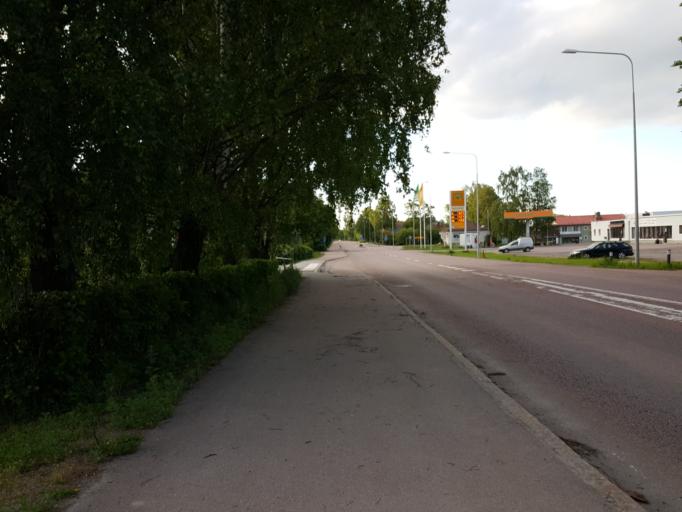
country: SE
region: Uppsala
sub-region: Osthammars Kommun
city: Gimo
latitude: 60.1675
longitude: 18.1935
